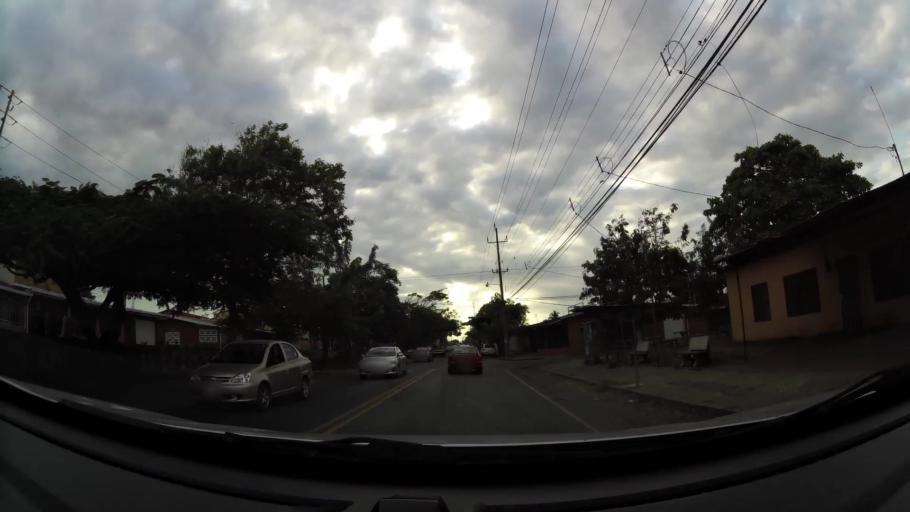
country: CR
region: Puntarenas
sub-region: Canton Central de Puntarenas
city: Puntarenas
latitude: 9.9801
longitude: -84.8162
